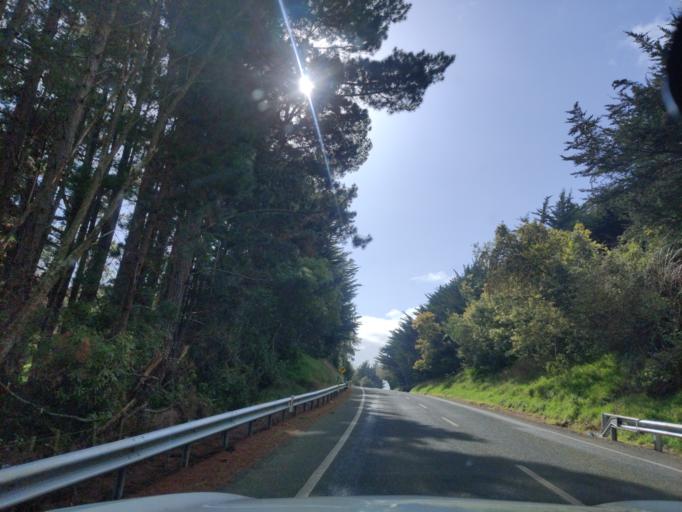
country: NZ
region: Manawatu-Wanganui
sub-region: Palmerston North City
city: Palmerston North
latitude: -40.4023
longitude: 175.6200
